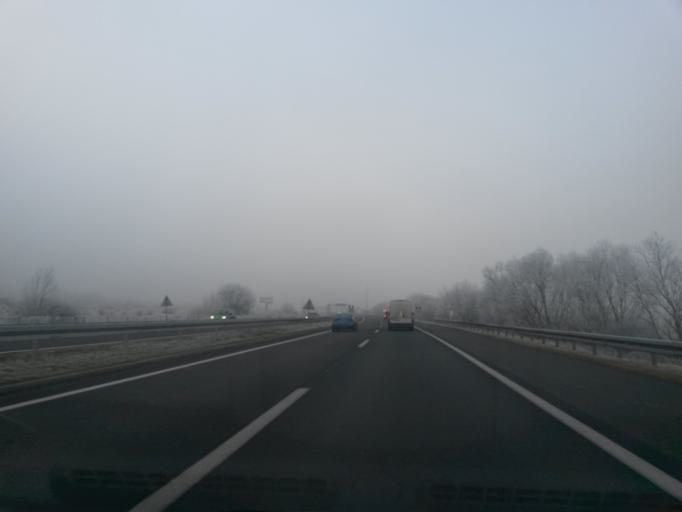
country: HR
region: Zagrebacka
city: Brckovljani
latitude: 45.9146
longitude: 16.2753
